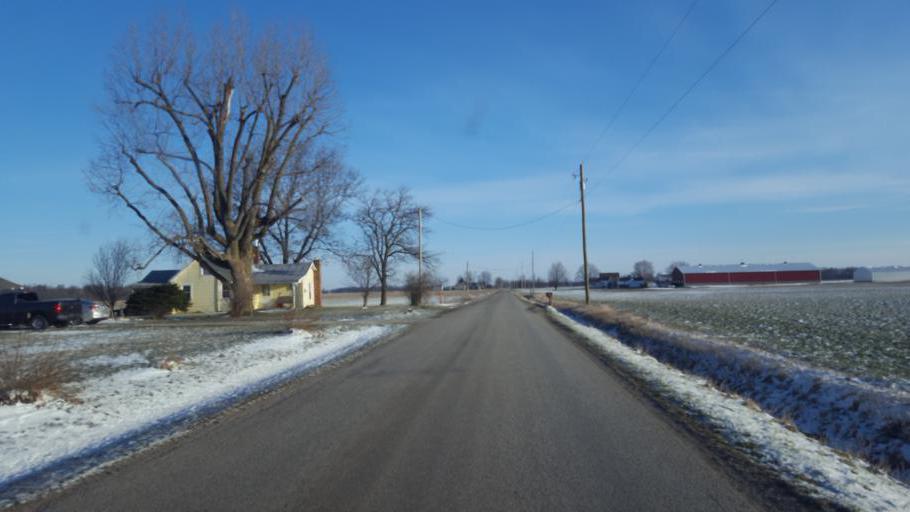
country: US
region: Ohio
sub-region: Morrow County
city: Cardington
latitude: 40.5927
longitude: -82.9186
